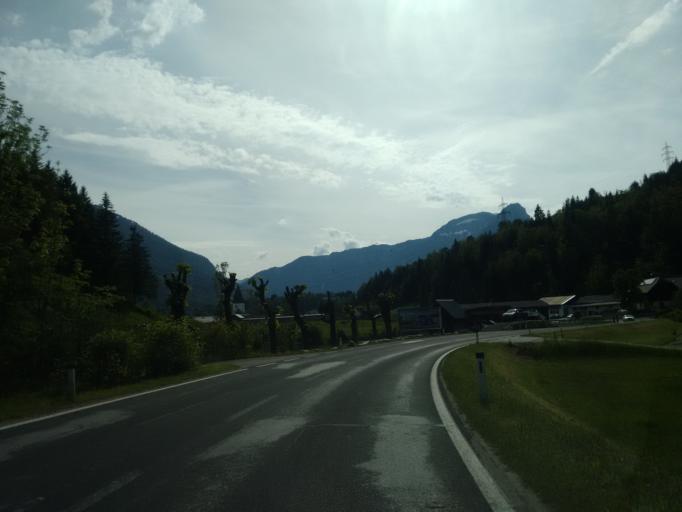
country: AT
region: Styria
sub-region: Politischer Bezirk Liezen
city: Bad Aussee
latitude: 47.6147
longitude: 13.7938
